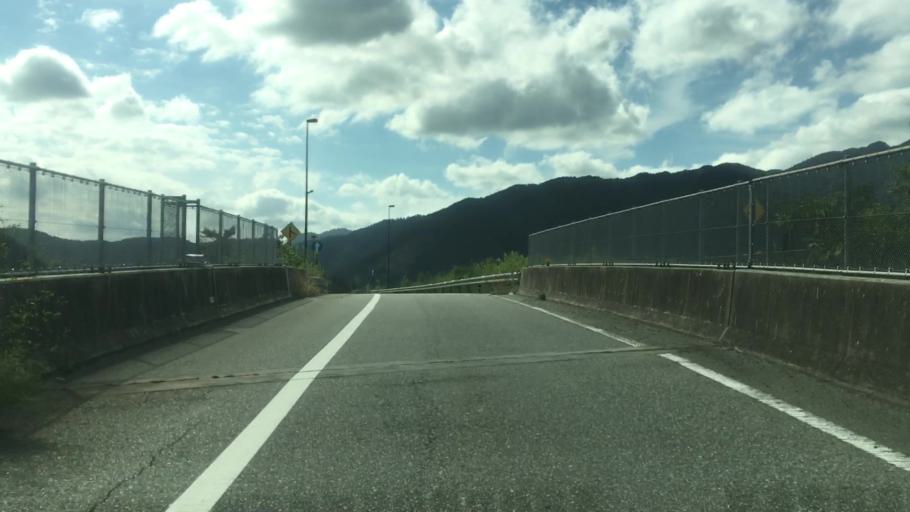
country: JP
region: Kyoto
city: Fukuchiyama
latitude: 35.2428
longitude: 135.0137
